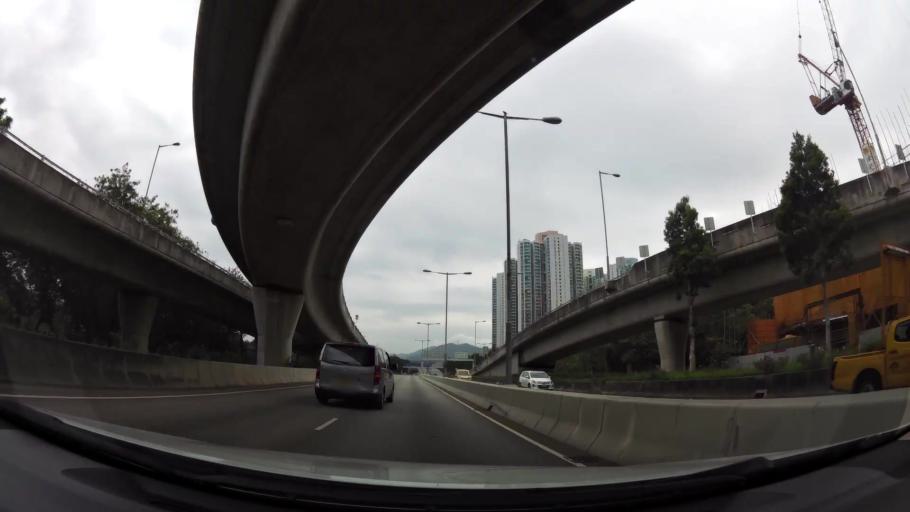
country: HK
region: Yuen Long
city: Yuen Long Kau Hui
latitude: 22.4562
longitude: 114.0091
